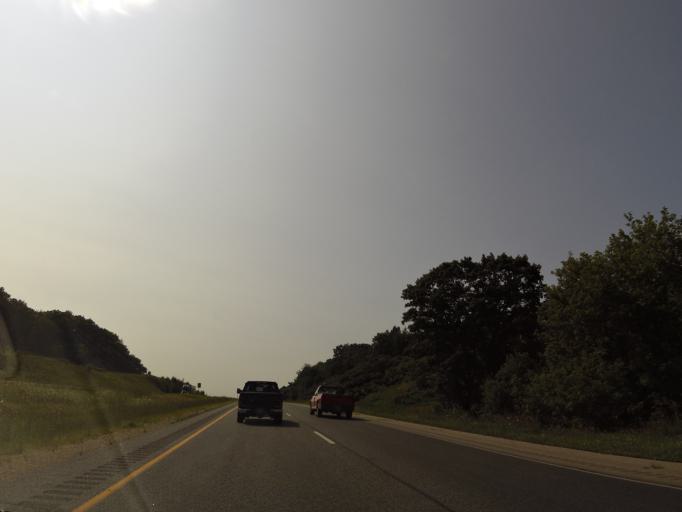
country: US
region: Wisconsin
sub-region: Monroe County
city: Tomah
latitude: 43.9394
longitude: -90.6010
